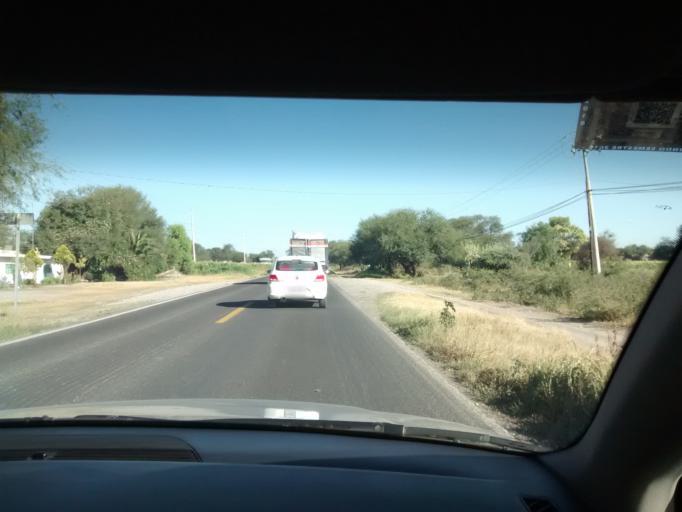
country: MX
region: Puebla
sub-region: Tehuacan
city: Magdalena Cuayucatepec
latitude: 18.5217
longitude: -97.5082
